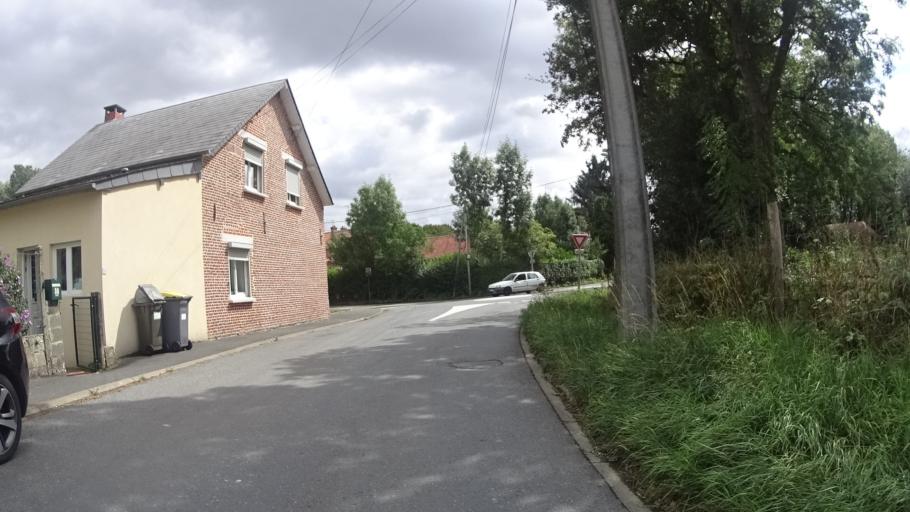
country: FR
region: Nord-Pas-de-Calais
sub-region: Departement du Nord
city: Pont-sur-Sambre
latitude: 50.2124
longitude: 3.8520
